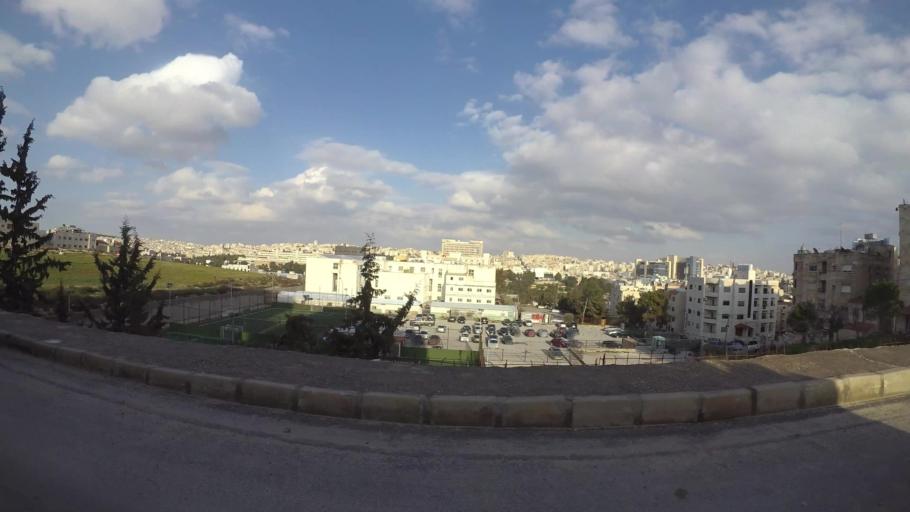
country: JO
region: Amman
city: Al Jubayhah
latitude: 32.0061
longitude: 35.8684
